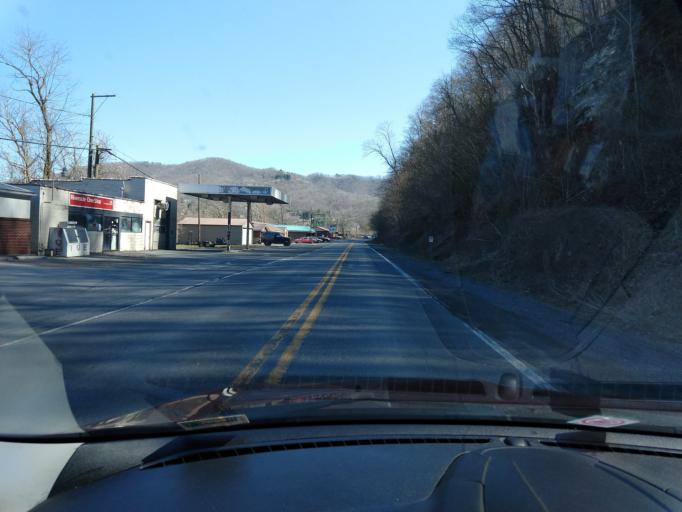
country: US
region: West Virginia
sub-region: Summers County
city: Hinton
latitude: 37.6529
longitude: -80.8910
